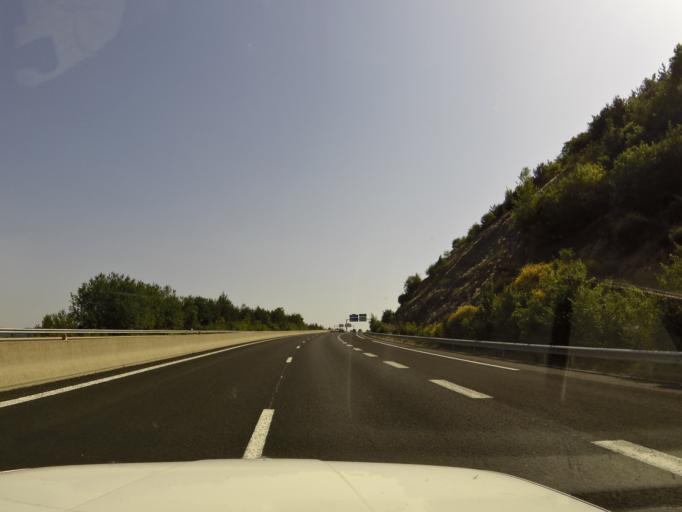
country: FR
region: Languedoc-Roussillon
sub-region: Departement de la Lozere
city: Chirac
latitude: 44.5054
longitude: 3.2439
